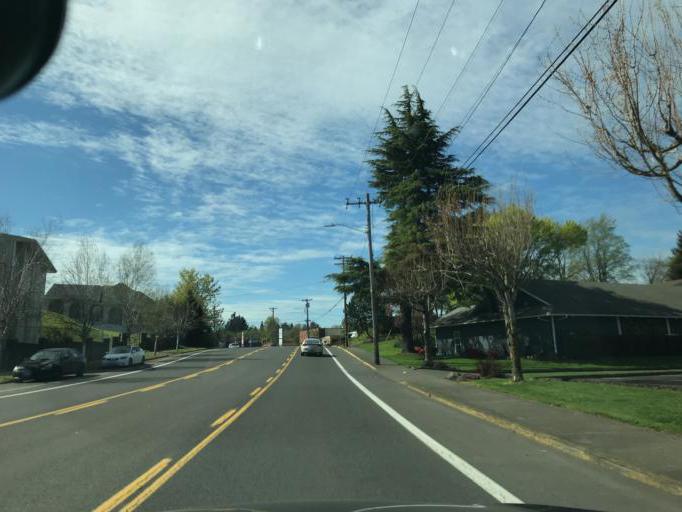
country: US
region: Oregon
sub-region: Multnomah County
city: Lents
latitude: 45.4992
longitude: -122.5681
